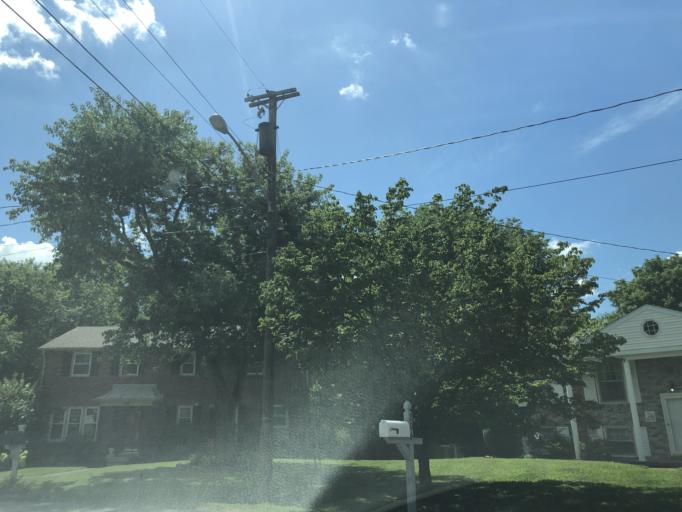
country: US
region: Tennessee
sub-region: Davidson County
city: Oak Hill
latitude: 36.0753
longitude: -86.7355
